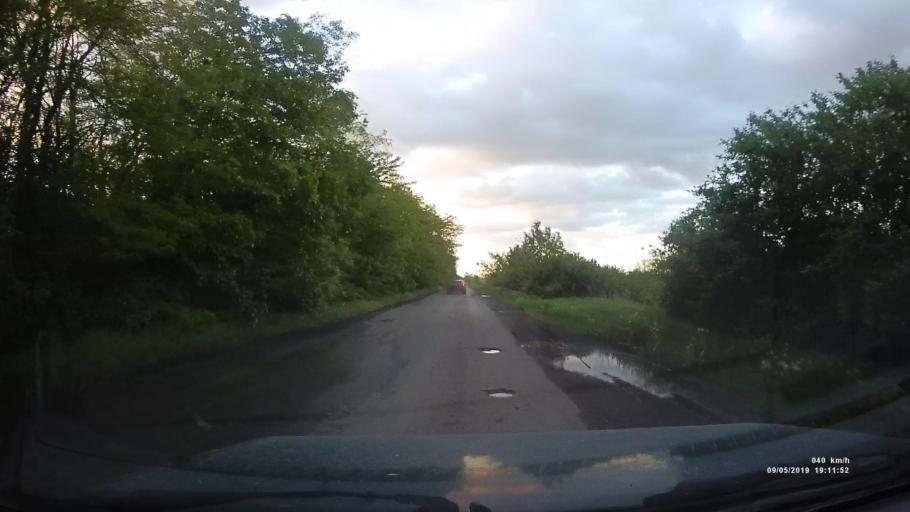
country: RU
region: Krasnodarskiy
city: Kanelovskaya
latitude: 46.7379
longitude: 39.2136
